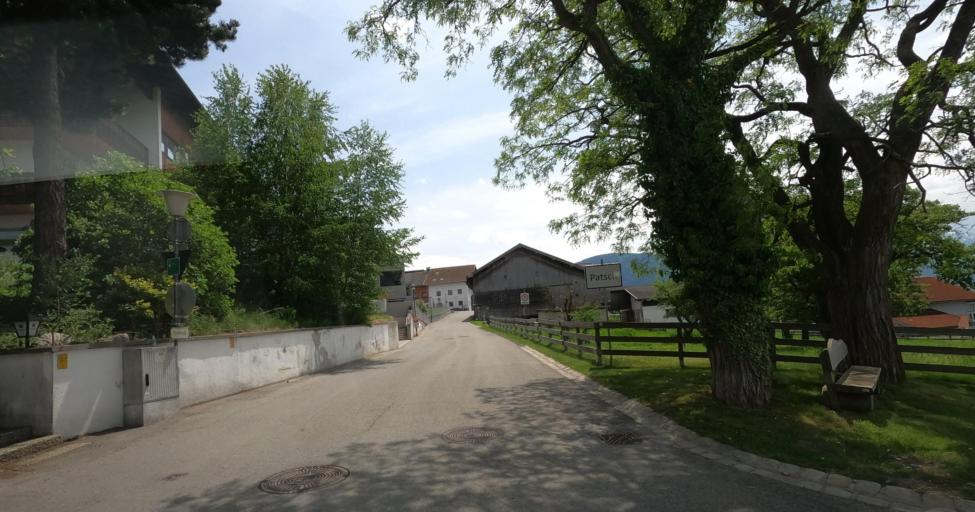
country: AT
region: Tyrol
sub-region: Politischer Bezirk Innsbruck Land
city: Patsch
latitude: 47.2065
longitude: 11.4129
